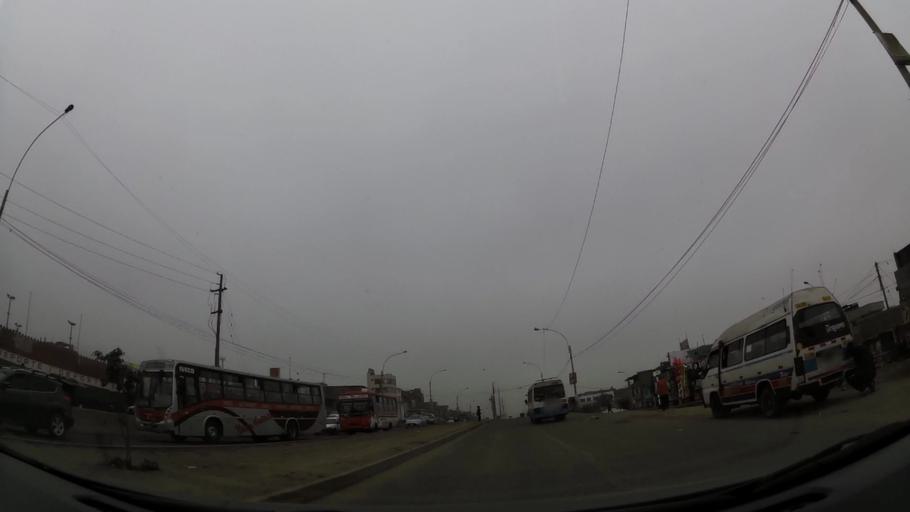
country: PE
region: Lima
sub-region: Lima
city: Urb. Santo Domingo
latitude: -11.8710
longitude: -77.0142
